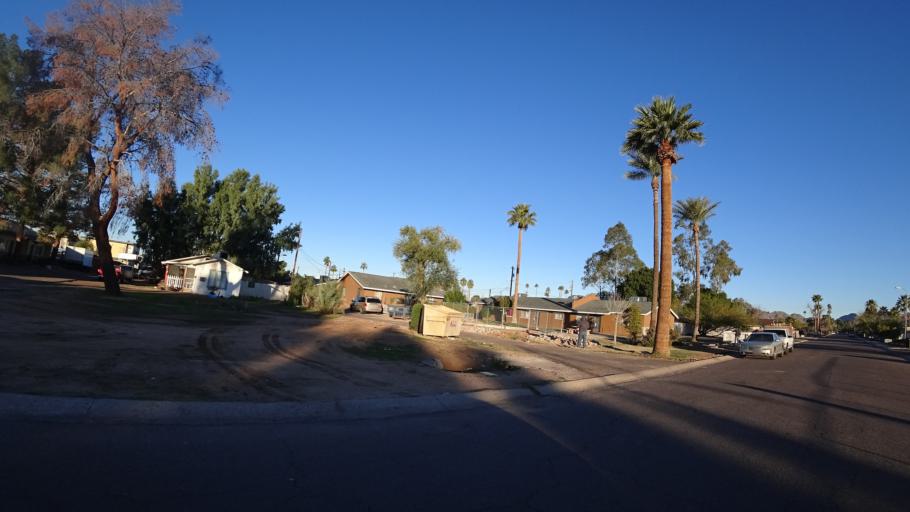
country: US
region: Arizona
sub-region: Maricopa County
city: Paradise Valley
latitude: 33.4853
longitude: -112.0020
